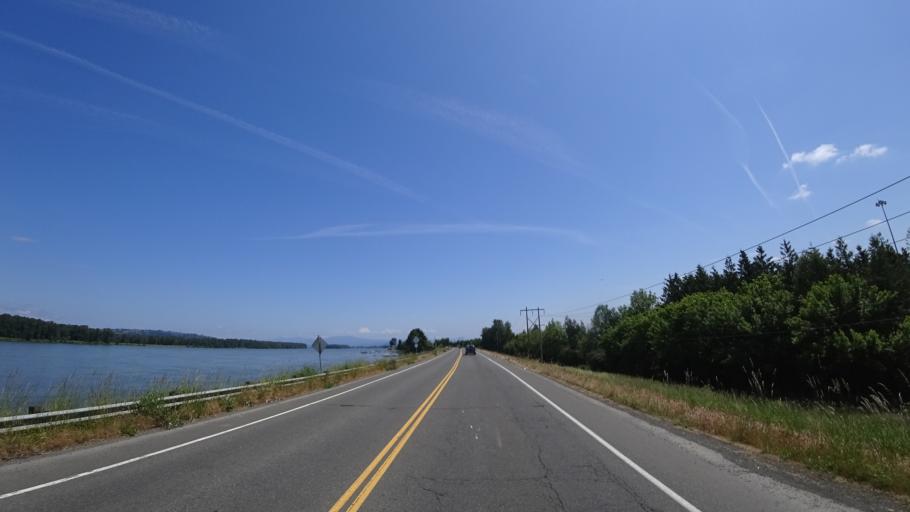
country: US
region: Washington
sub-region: Clark County
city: Mill Plain
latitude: 45.5670
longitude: -122.5297
